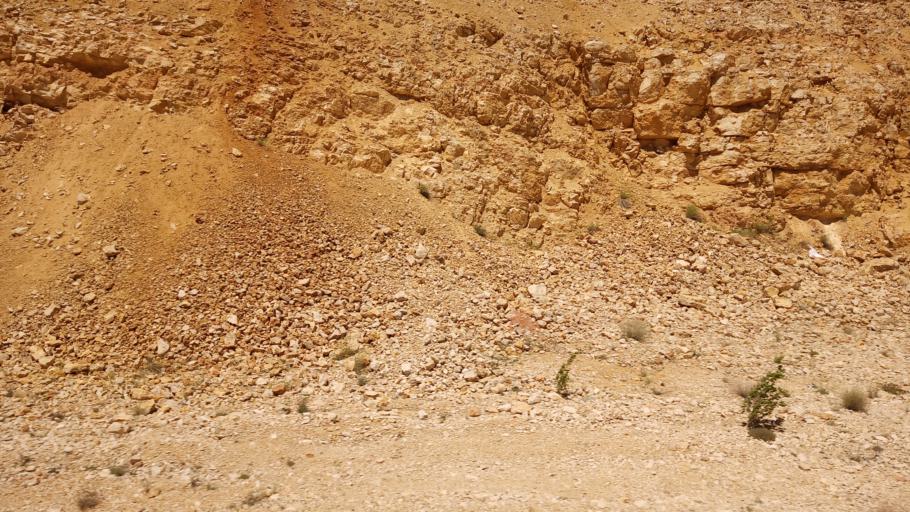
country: TR
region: Malatya
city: Darende
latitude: 38.6265
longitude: 37.4566
